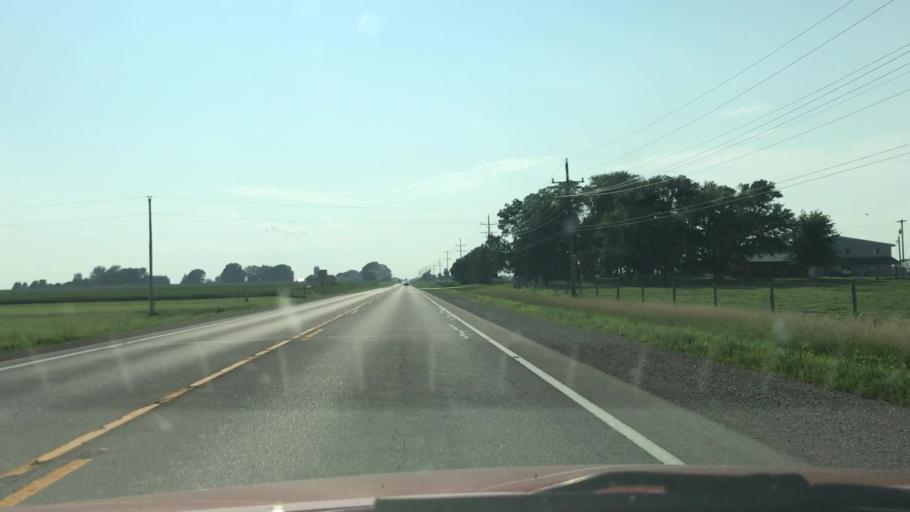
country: US
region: Wisconsin
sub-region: Outagamie County
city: Seymour
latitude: 44.5010
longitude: -88.2985
